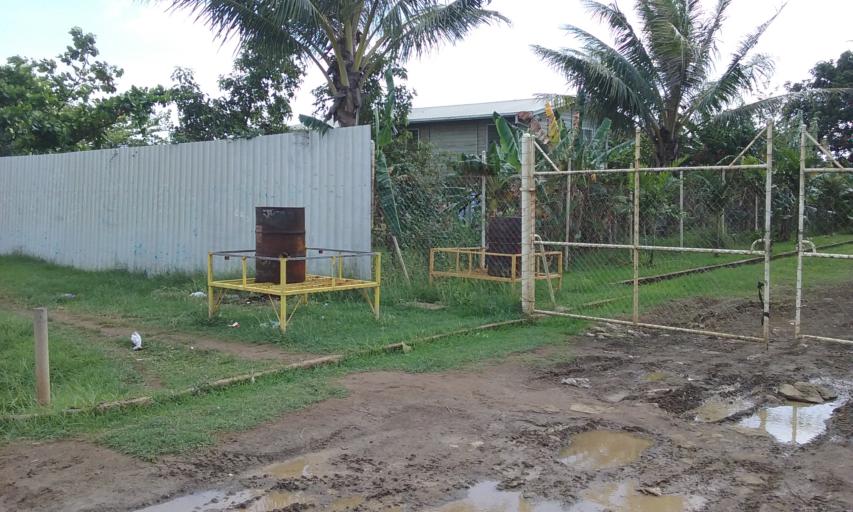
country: PG
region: Western Province
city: Daru
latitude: -9.0819
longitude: 143.2042
